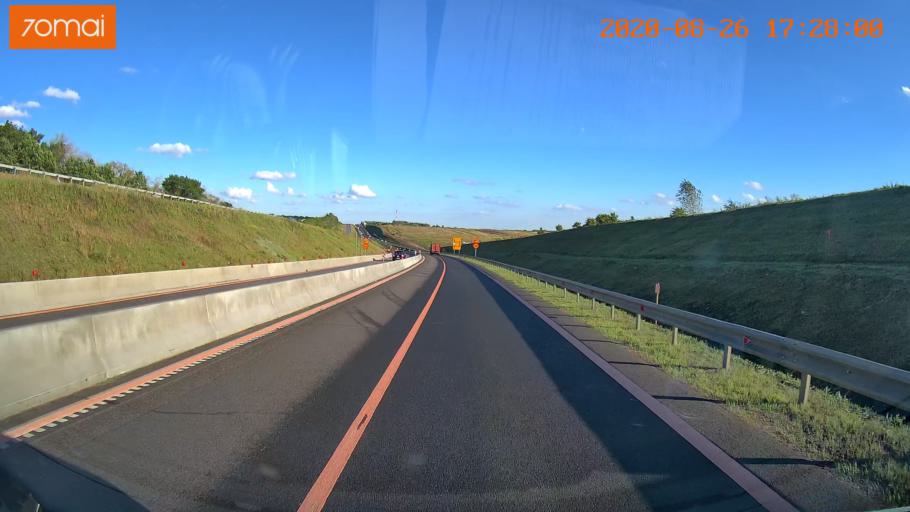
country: RU
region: Tula
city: Kazachka
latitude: 53.4672
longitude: 38.1282
